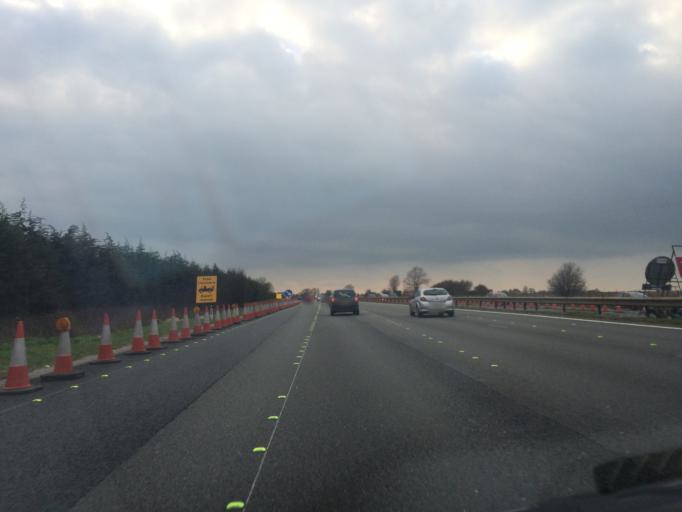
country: GB
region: England
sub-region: West Berkshire
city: Winterbourne
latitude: 51.4564
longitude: -1.3528
